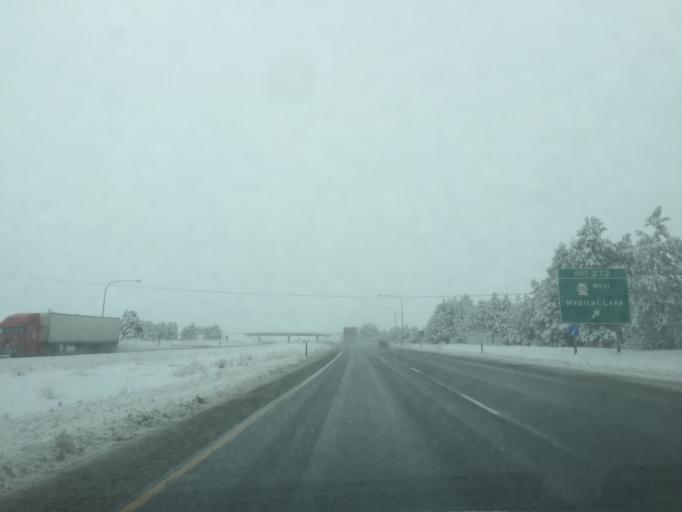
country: US
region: Washington
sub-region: Spokane County
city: Airway Heights
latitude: 47.5949
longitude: -117.5605
